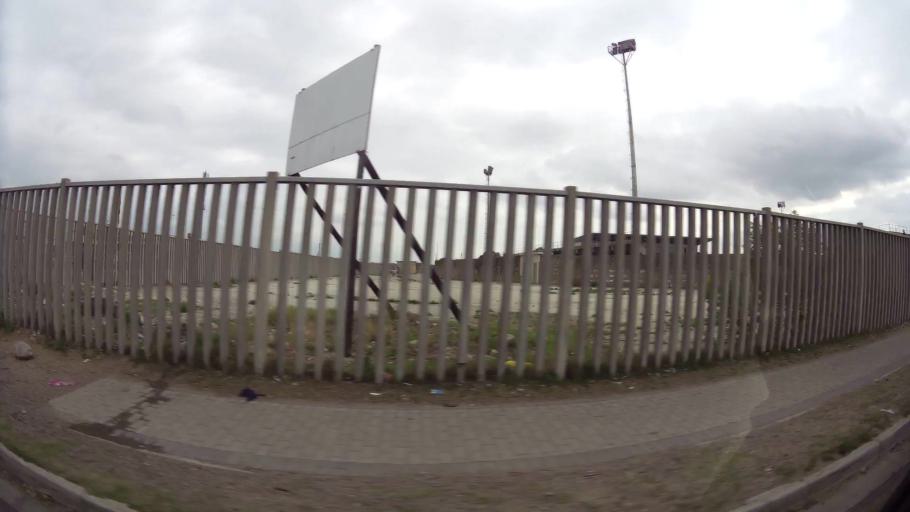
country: ZA
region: Eastern Cape
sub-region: Nelson Mandela Bay Metropolitan Municipality
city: Port Elizabeth
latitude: -33.8852
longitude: 25.5959
